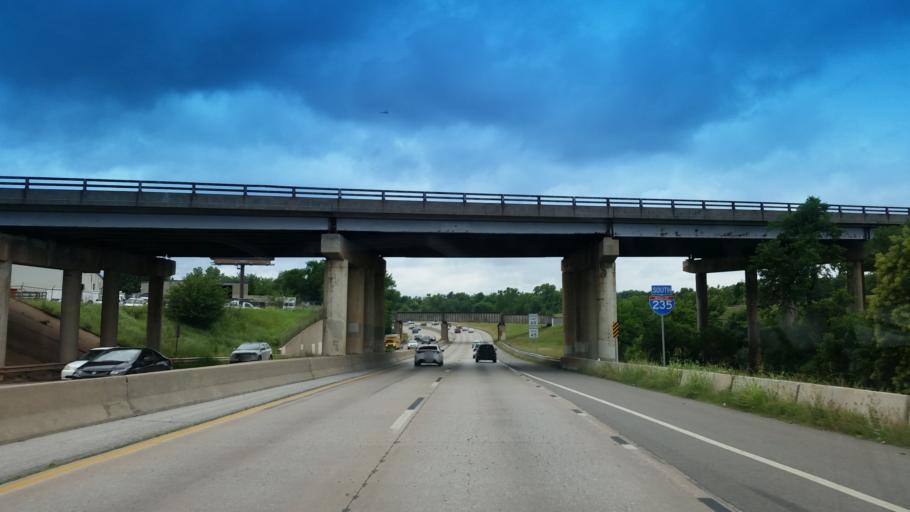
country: US
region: Oklahoma
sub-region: Oklahoma County
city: Nichols Hills
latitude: 35.5230
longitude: -97.5165
